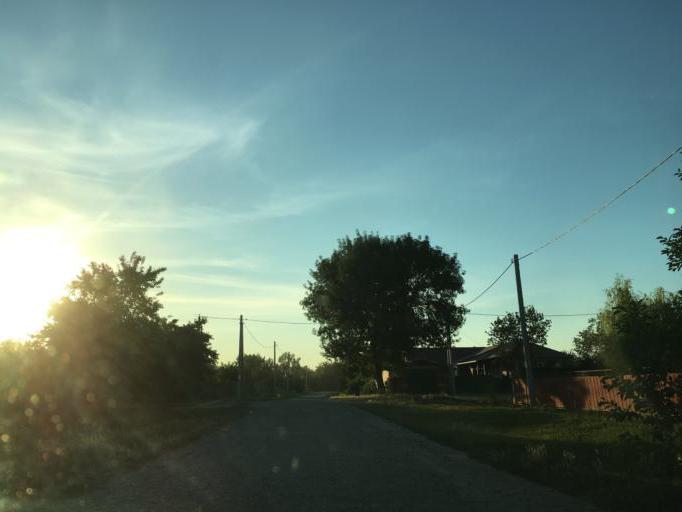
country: RU
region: Krasnodarskiy
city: Kushchevskaya
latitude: 46.5644
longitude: 39.6511
